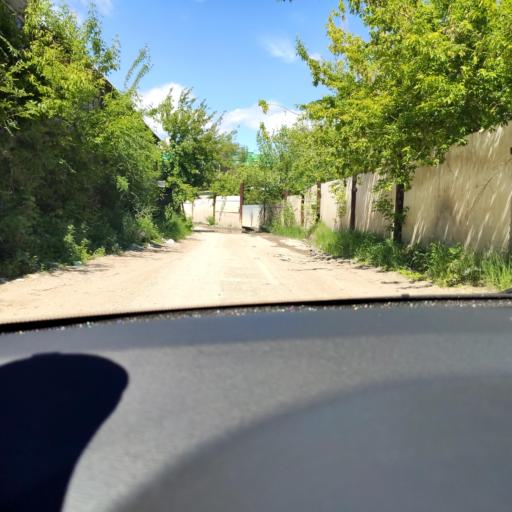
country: RU
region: Samara
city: Samara
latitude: 53.1787
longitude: 50.2116
